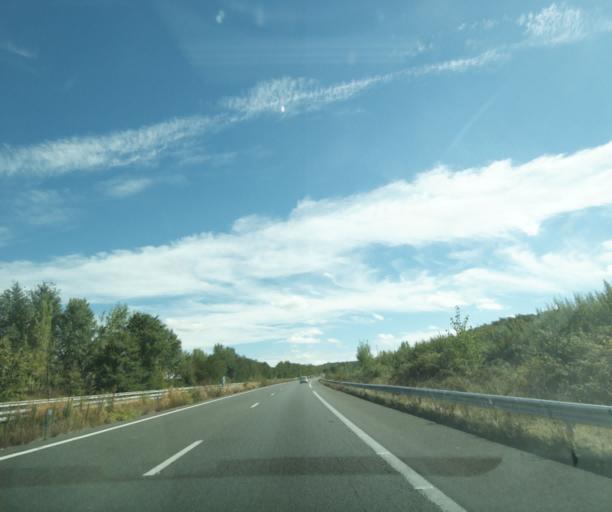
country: FR
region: Midi-Pyrenees
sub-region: Departement du Tarn-et-Garonne
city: Lamagistere
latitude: 44.0919
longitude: 0.7886
